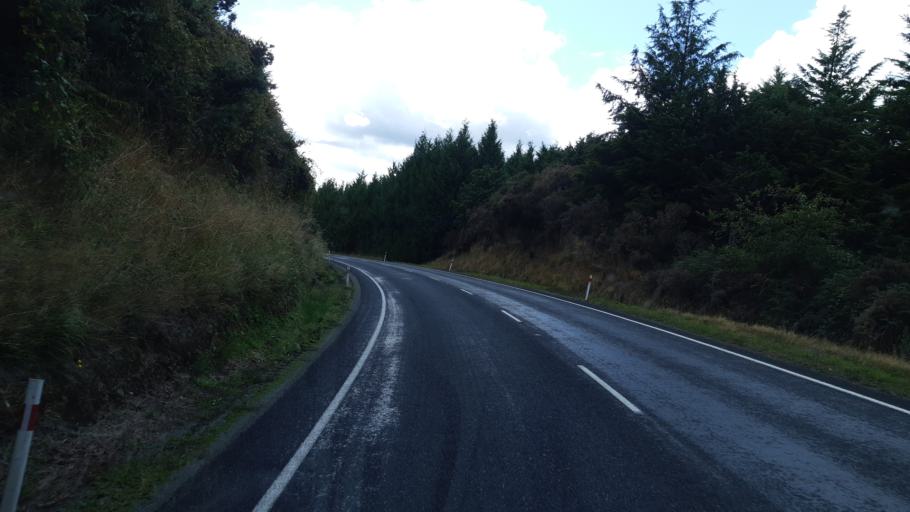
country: NZ
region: Tasman
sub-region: Tasman District
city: Wakefield
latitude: -41.5543
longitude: 172.7884
